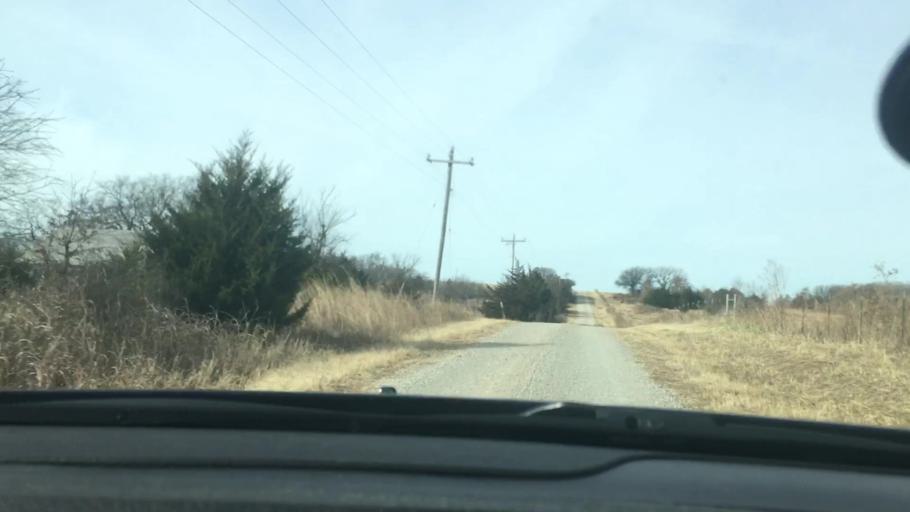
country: US
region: Oklahoma
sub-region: Garvin County
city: Wynnewood
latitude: 34.6374
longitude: -97.2387
